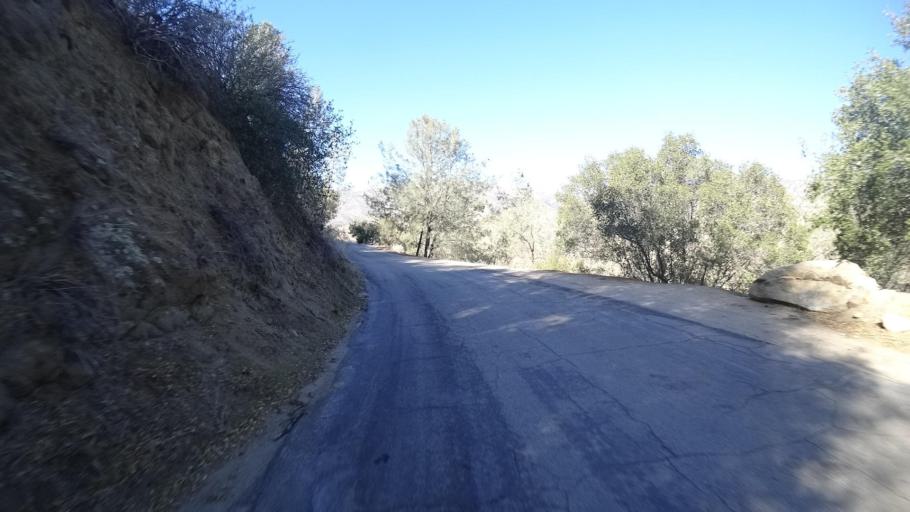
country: US
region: California
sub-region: Kern County
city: Bodfish
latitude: 35.5526
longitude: -118.6043
